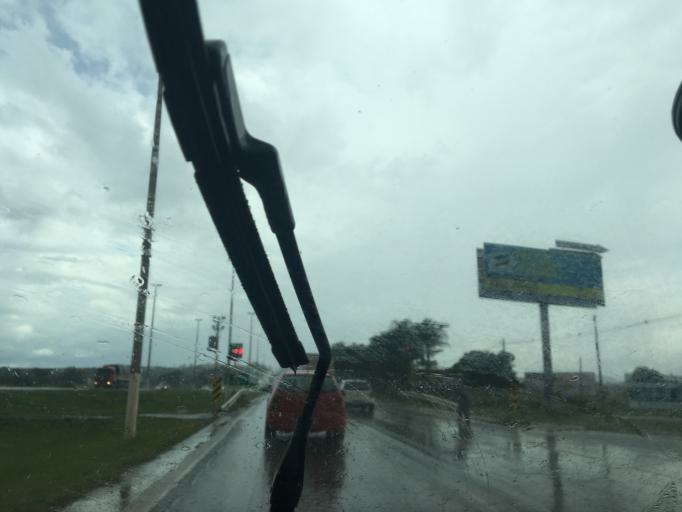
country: BR
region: Goias
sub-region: Luziania
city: Luziania
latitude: -16.1767
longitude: -47.9294
